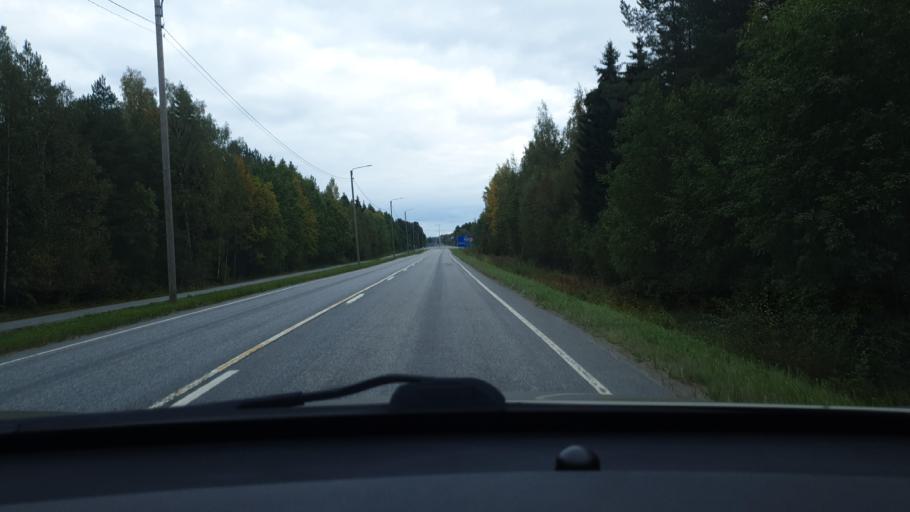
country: FI
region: Ostrobothnia
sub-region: Vaasa
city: Ristinummi
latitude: 63.0577
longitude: 21.7146
